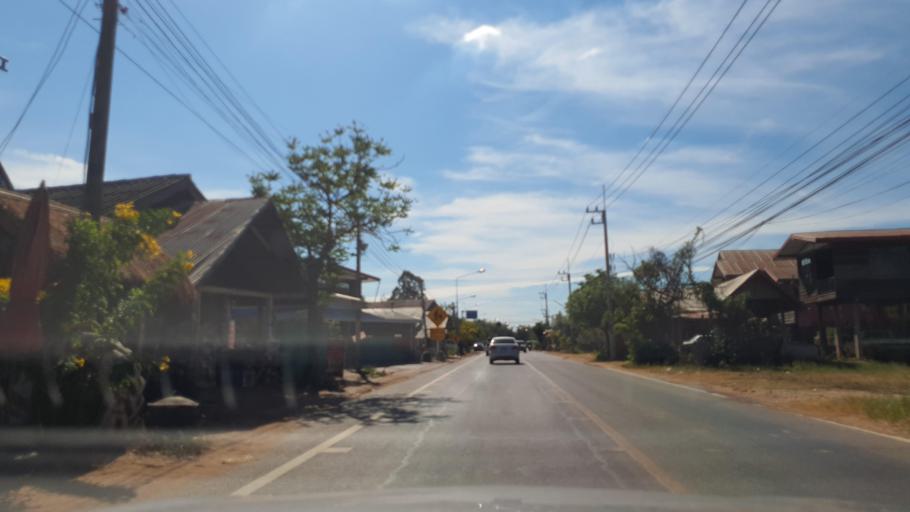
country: TH
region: Kalasin
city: Khao Wong
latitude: 16.7344
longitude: 104.0972
